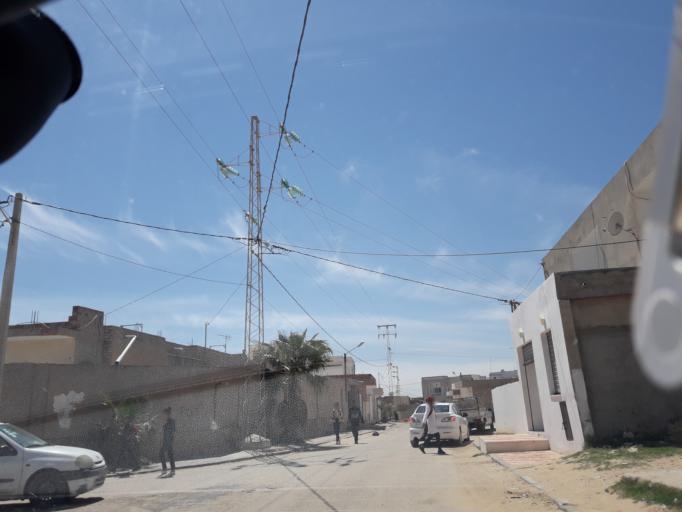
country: TN
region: Safaqis
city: Sfax
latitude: 34.7416
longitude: 10.5242
